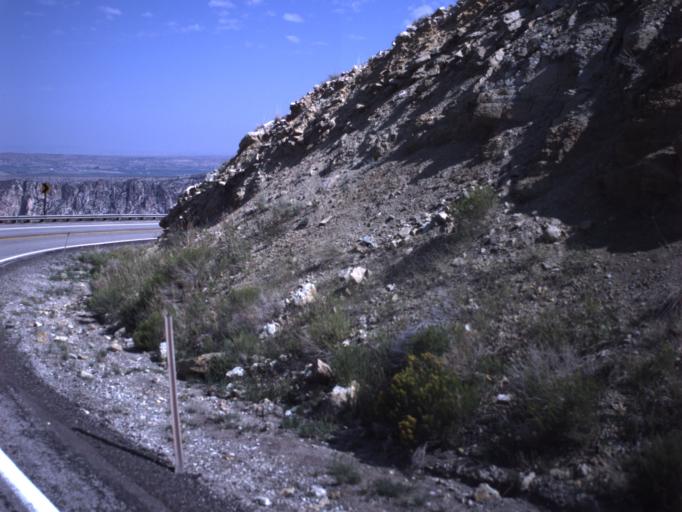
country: US
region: Utah
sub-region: Daggett County
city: Manila
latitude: 40.9088
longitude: -109.7009
